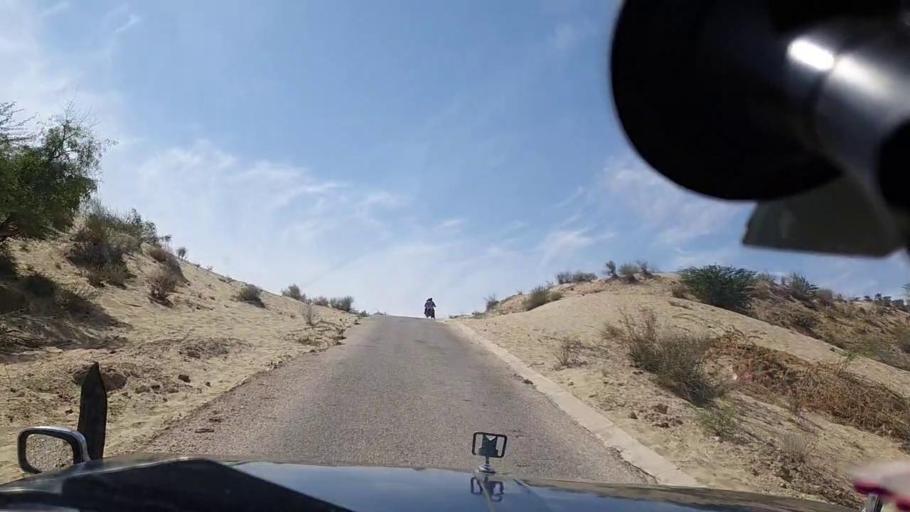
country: PK
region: Sindh
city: Diplo
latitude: 24.3951
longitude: 69.5884
